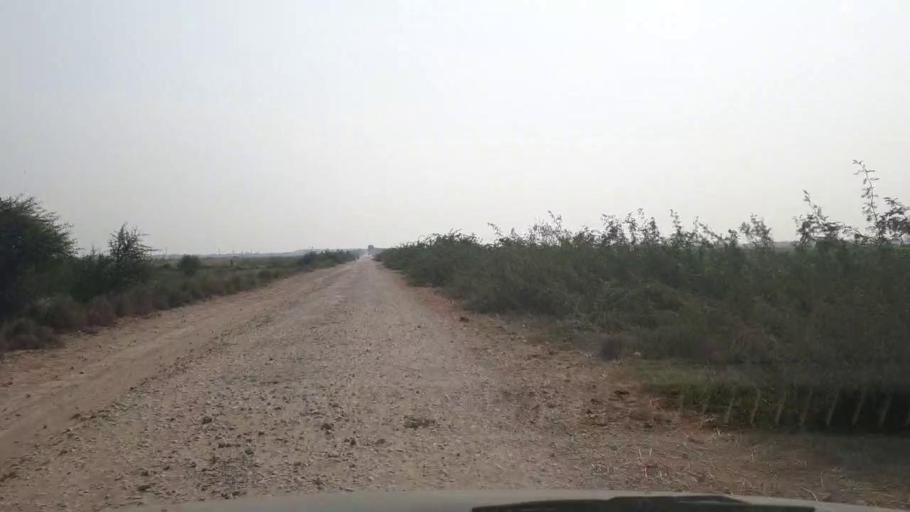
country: PK
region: Sindh
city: Tando Muhammad Khan
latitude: 25.0500
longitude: 68.3886
